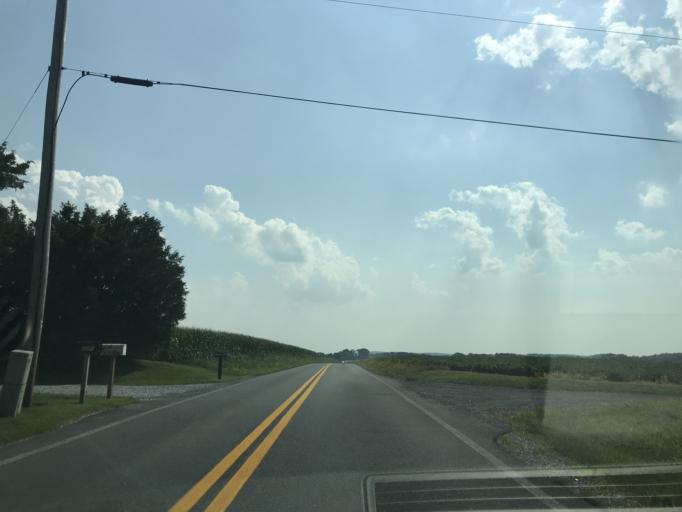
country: US
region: Maryland
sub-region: Carroll County
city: Westminster
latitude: 39.6318
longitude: -76.9591
